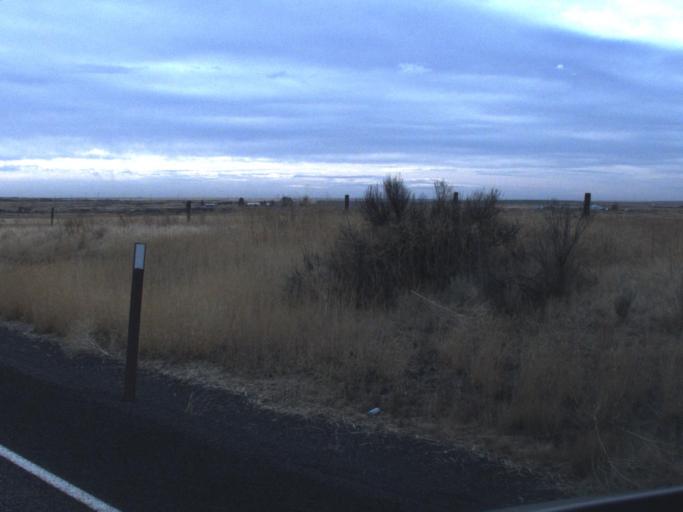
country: US
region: Washington
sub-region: Okanogan County
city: Coulee Dam
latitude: 47.7769
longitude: -118.7289
